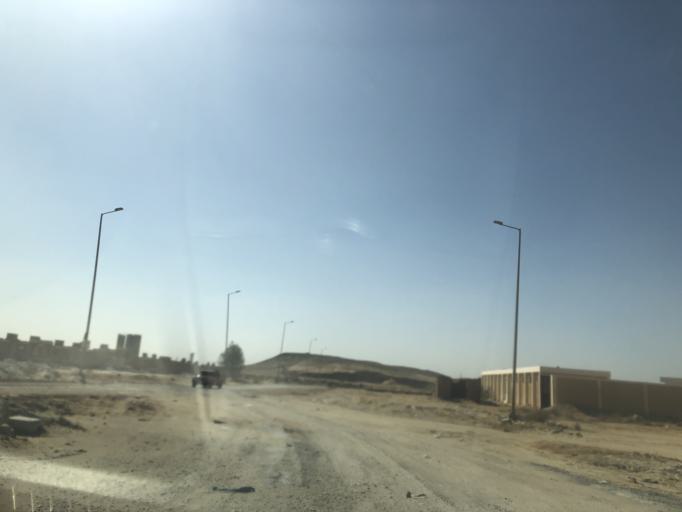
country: EG
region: Al Jizah
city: Madinat Sittah Uktubar
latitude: 29.9332
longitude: 30.9579
